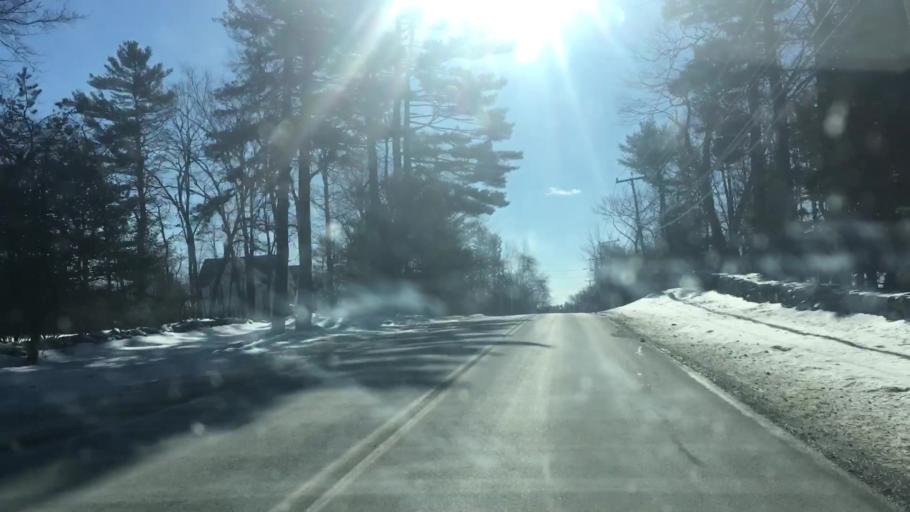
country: US
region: Maine
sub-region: Hancock County
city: Ellsworth
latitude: 44.5353
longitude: -68.4310
